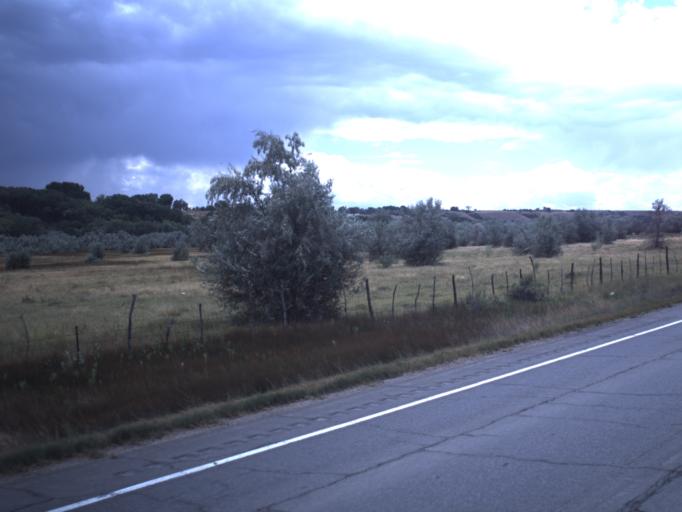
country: US
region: Utah
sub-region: Duchesne County
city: Roosevelt
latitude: 40.1780
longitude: -110.1186
